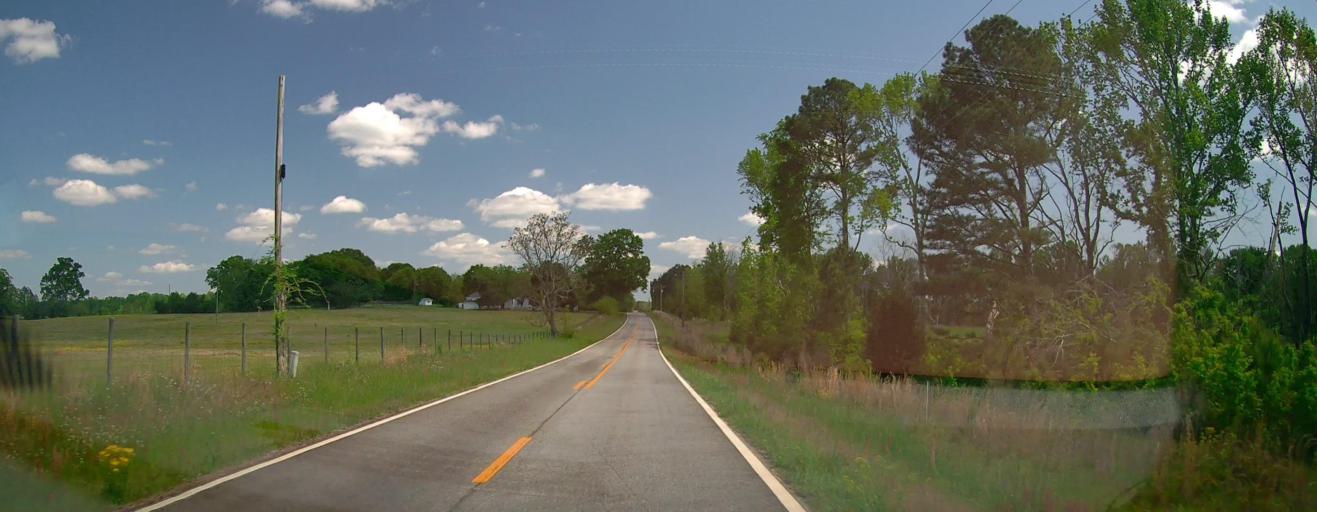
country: US
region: Georgia
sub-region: Putnam County
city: Eatonton
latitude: 33.3295
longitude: -83.3168
